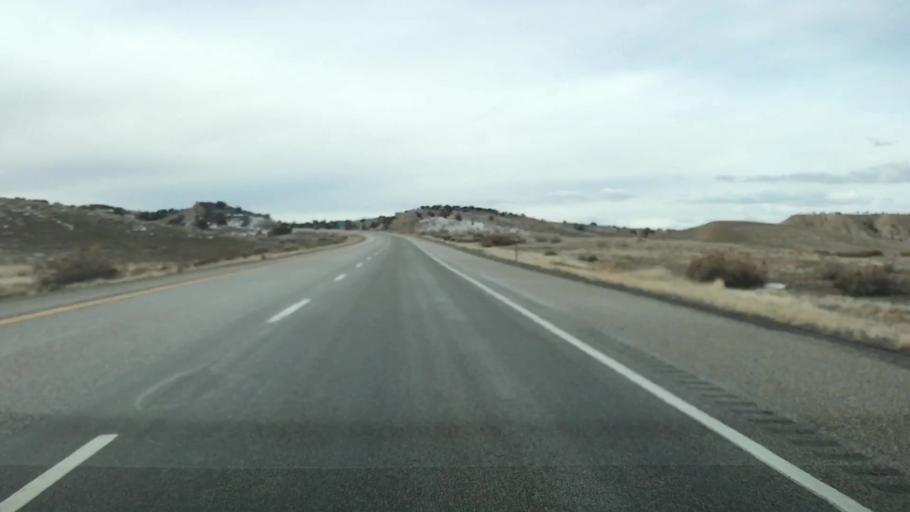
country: US
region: Colorado
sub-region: Mesa County
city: Loma
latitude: 39.1902
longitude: -109.1054
